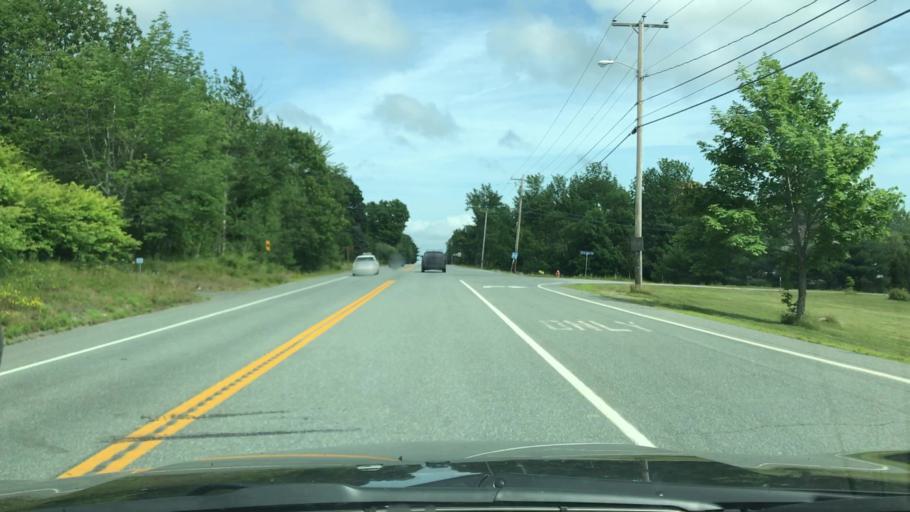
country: US
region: Maine
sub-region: Hancock County
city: Surry
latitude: 44.5451
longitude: -68.5173
